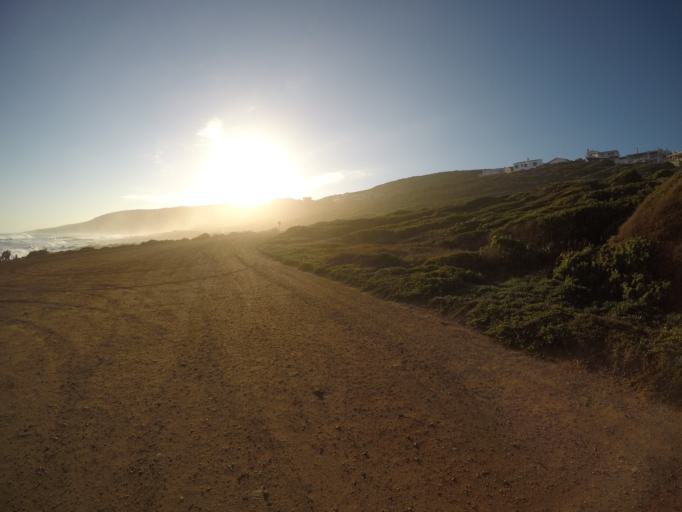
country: ZA
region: Western Cape
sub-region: Eden District Municipality
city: Riversdale
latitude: -34.4330
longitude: 21.3297
